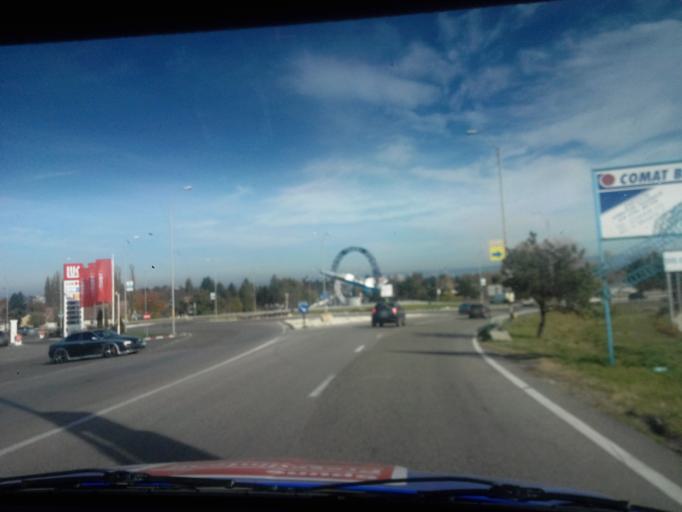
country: RO
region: Bacau
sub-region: Municipiul Bacau
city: Bacau
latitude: 46.5563
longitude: 26.8848
